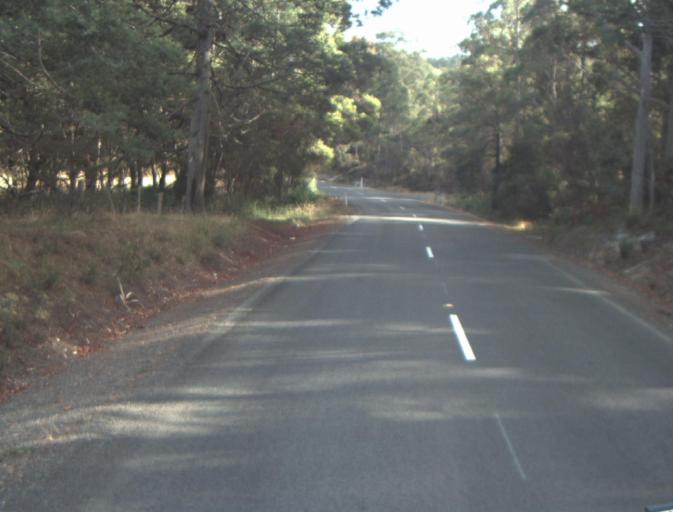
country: AU
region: Tasmania
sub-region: Dorset
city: Bridport
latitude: -41.1544
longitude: 147.2385
